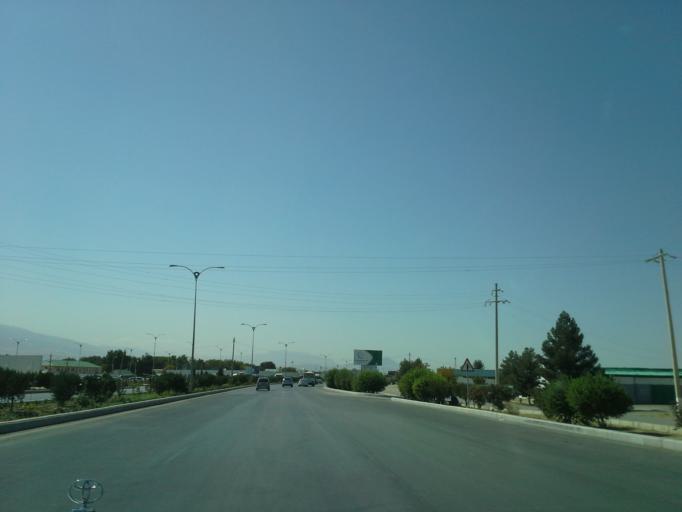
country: TM
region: Ahal
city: Annau
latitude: 37.9076
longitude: 58.5128
